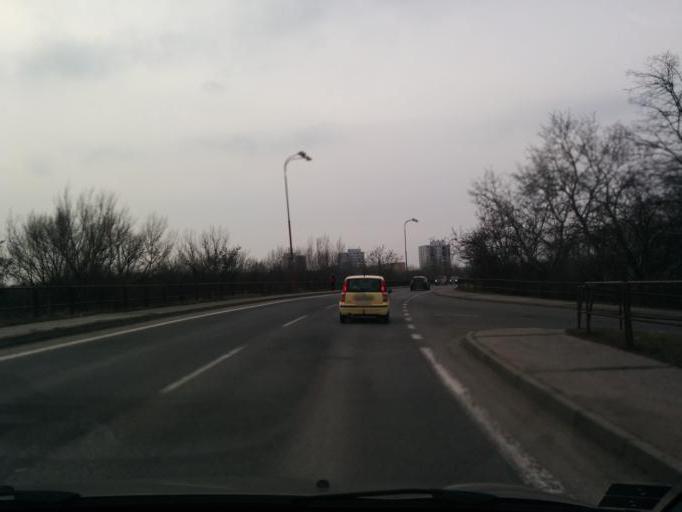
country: SK
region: Trnavsky
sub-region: Okres Galanta
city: Galanta
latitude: 48.2849
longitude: 17.7520
